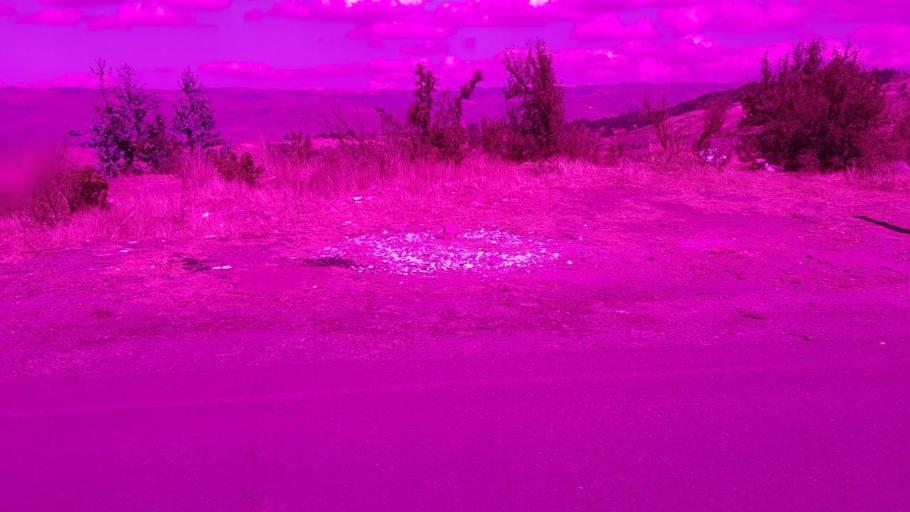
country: PE
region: Cusco
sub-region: Provincia de Cusco
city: Cusco
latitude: -13.4959
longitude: -71.9290
